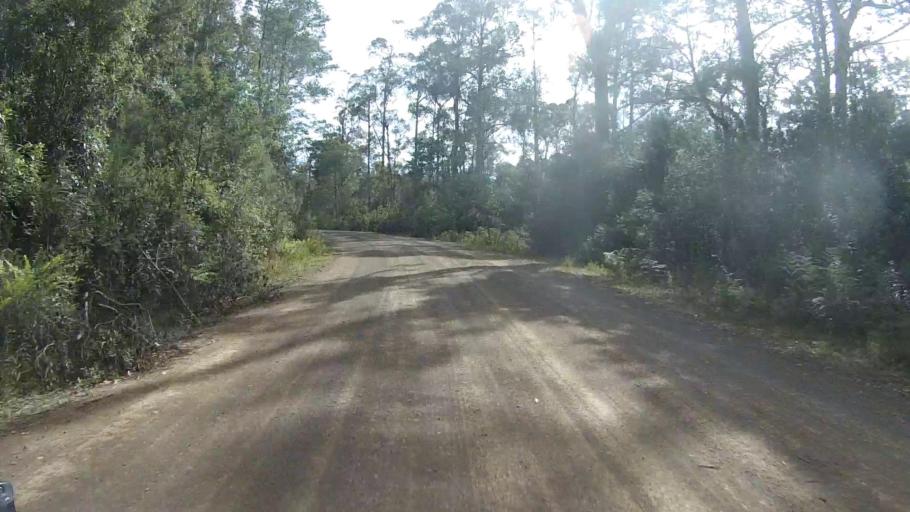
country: AU
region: Tasmania
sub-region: Sorell
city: Sorell
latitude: -42.7382
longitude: 147.8333
